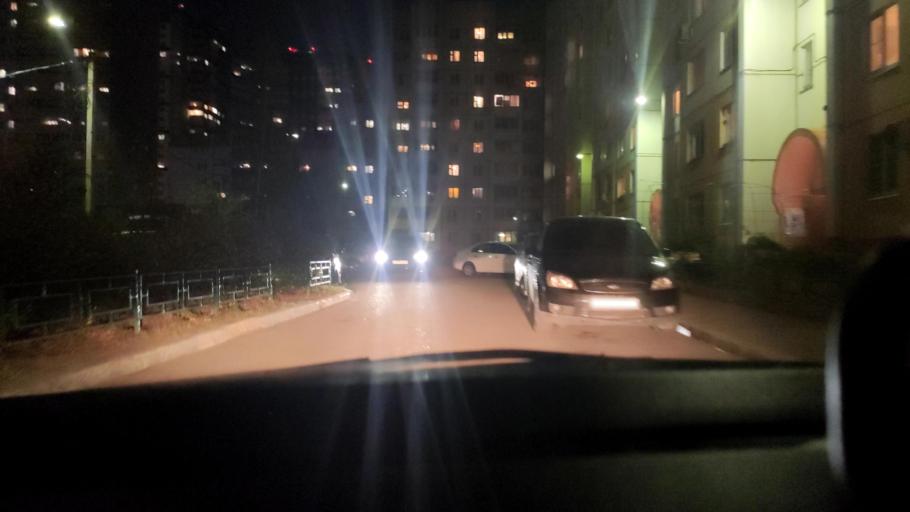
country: RU
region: Voronezj
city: Podgornoye
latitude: 51.7149
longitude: 39.1467
